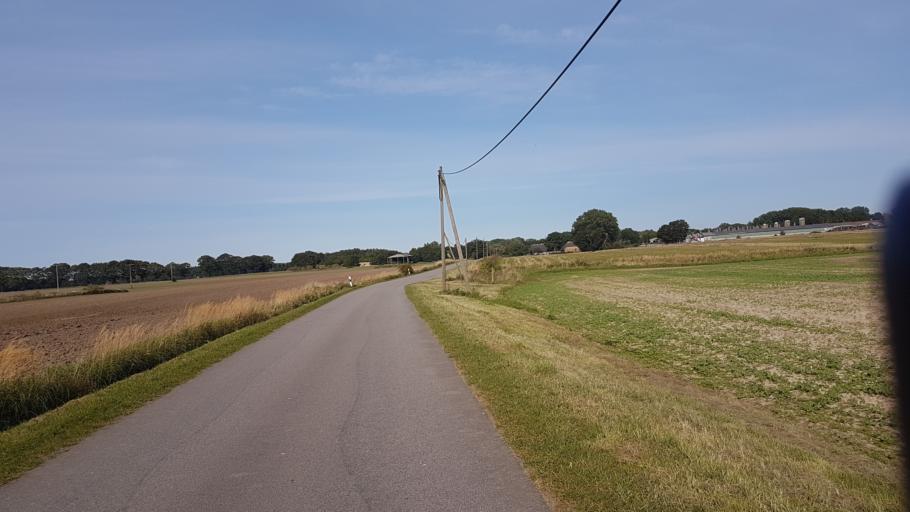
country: DE
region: Mecklenburg-Vorpommern
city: Gingst
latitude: 54.4307
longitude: 13.2232
